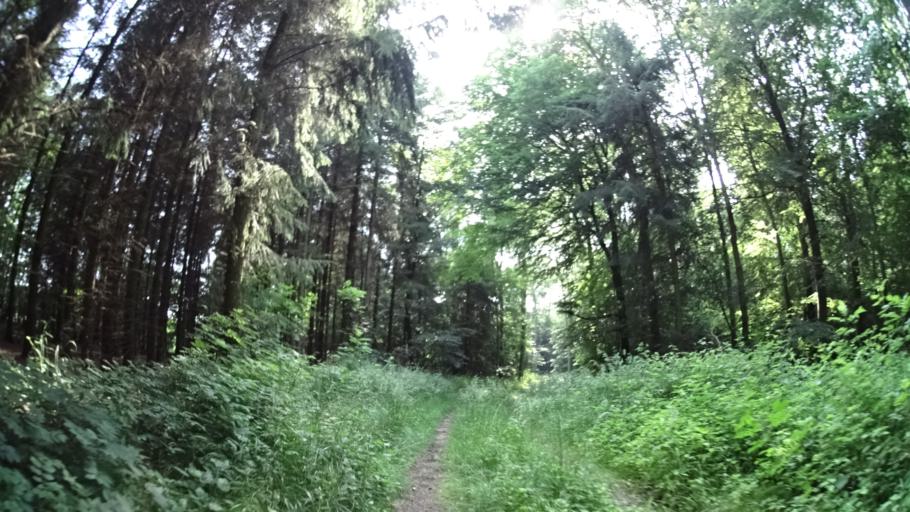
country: DK
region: Central Jutland
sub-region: Arhus Kommune
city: Stavtrup
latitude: 56.1405
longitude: 10.0992
